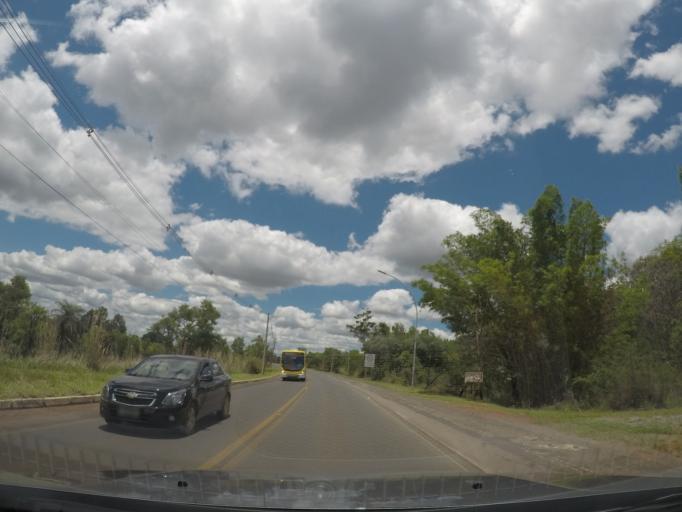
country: BR
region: Federal District
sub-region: Brasilia
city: Brasilia
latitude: -15.7832
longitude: -47.8059
